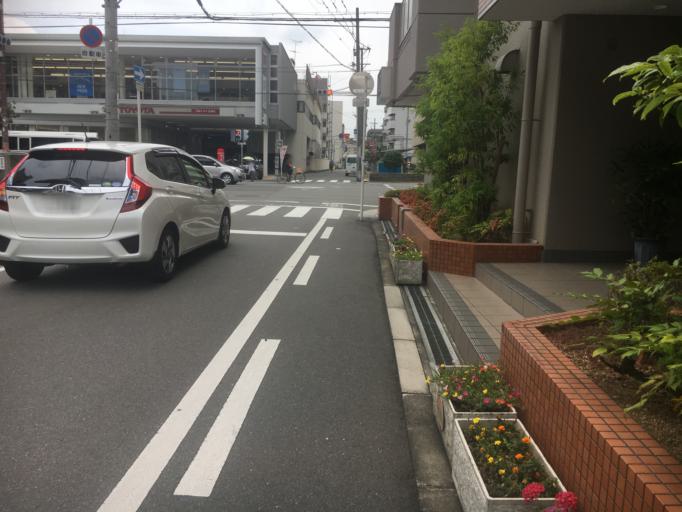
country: JP
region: Osaka
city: Yao
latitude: 34.6536
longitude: 135.5538
